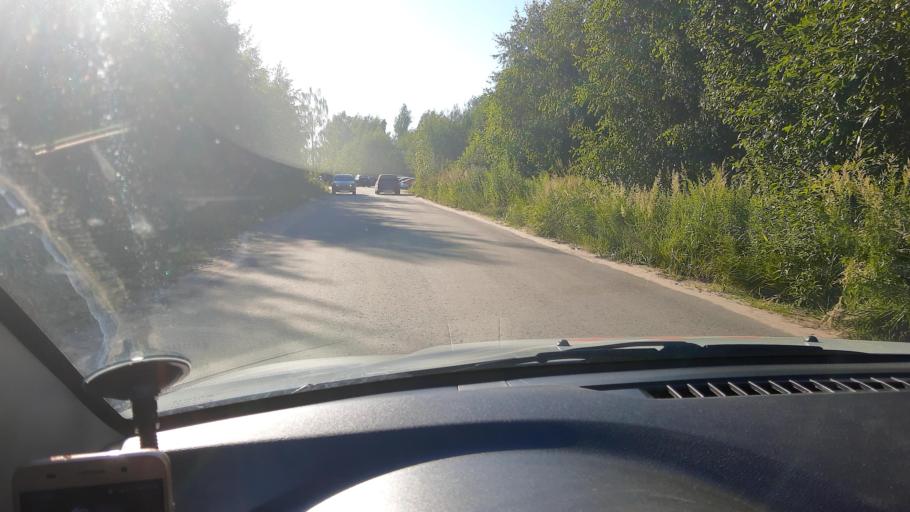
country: RU
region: Nizjnij Novgorod
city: Gorbatovka
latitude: 56.3647
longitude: 43.7807
